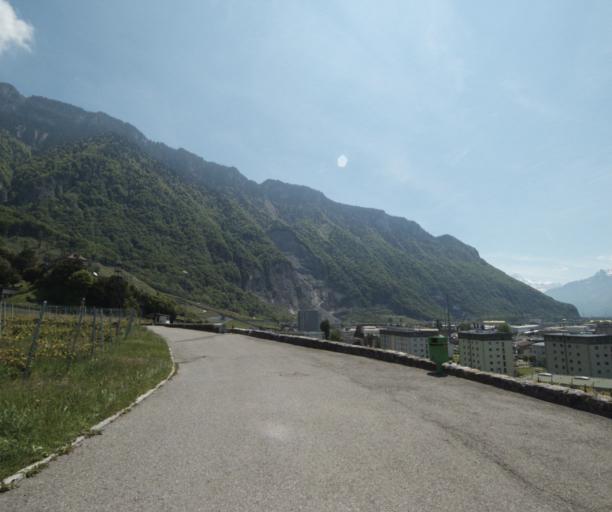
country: CH
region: Vaud
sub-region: Aigle District
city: Villeneuve
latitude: 46.3985
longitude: 6.9316
